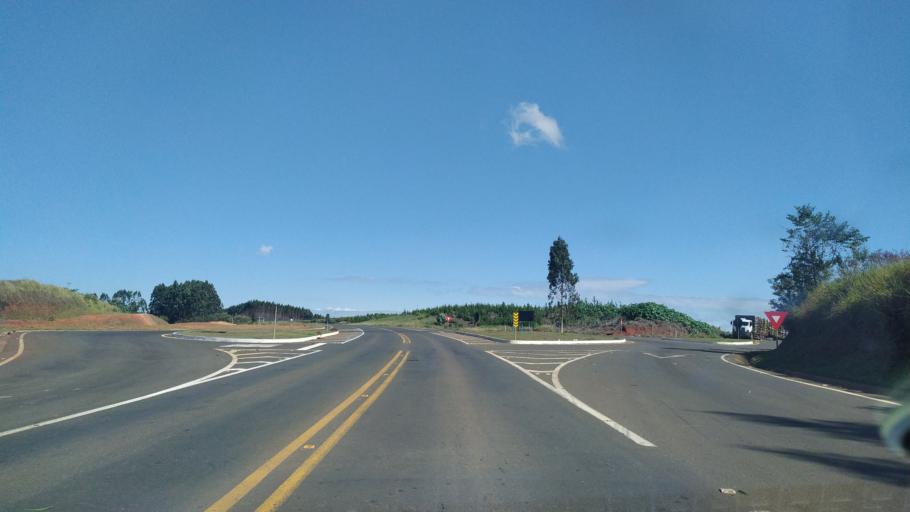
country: BR
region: Parana
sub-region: Telemaco Borba
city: Telemaco Borba
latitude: -24.2451
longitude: -50.7751
